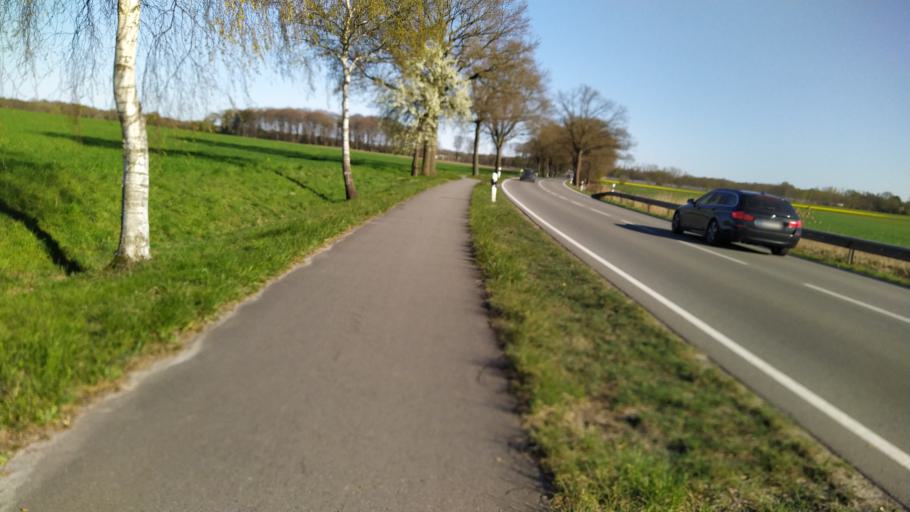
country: DE
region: Lower Saxony
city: Gross Meckelsen
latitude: 53.2883
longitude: 9.4650
